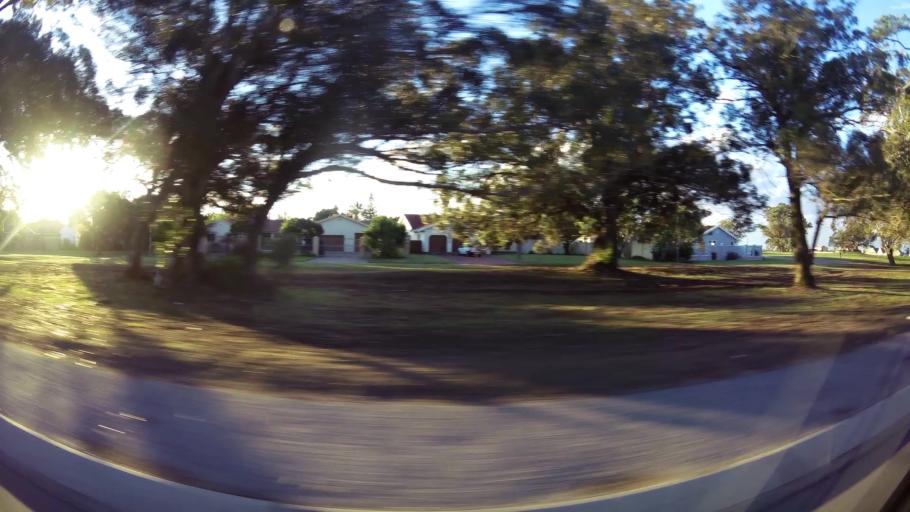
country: ZA
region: Eastern Cape
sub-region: Nelson Mandela Bay Metropolitan Municipality
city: Port Elizabeth
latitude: -33.9677
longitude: 25.4969
